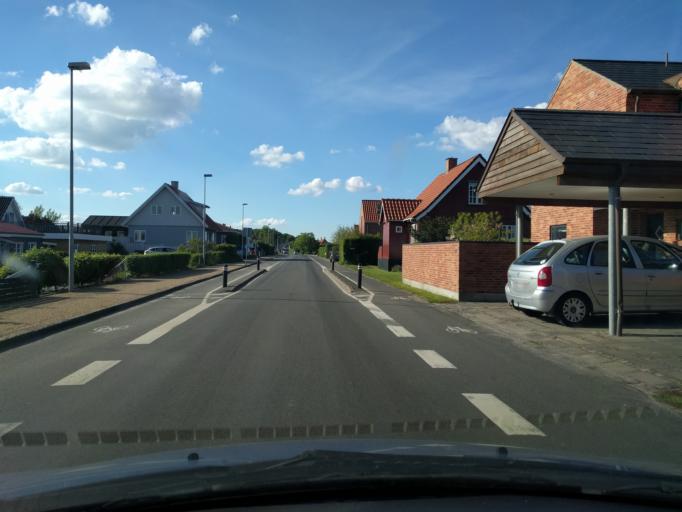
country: DK
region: South Denmark
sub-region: Nyborg Kommune
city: Nyborg
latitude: 55.3123
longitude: 10.8154
